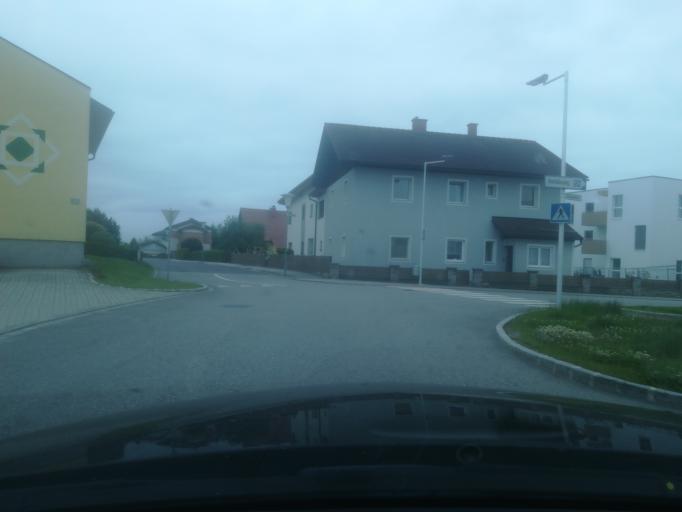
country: AT
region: Upper Austria
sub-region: Politischer Bezirk Urfahr-Umgebung
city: Engerwitzdorf
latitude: 48.3504
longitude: 14.5298
